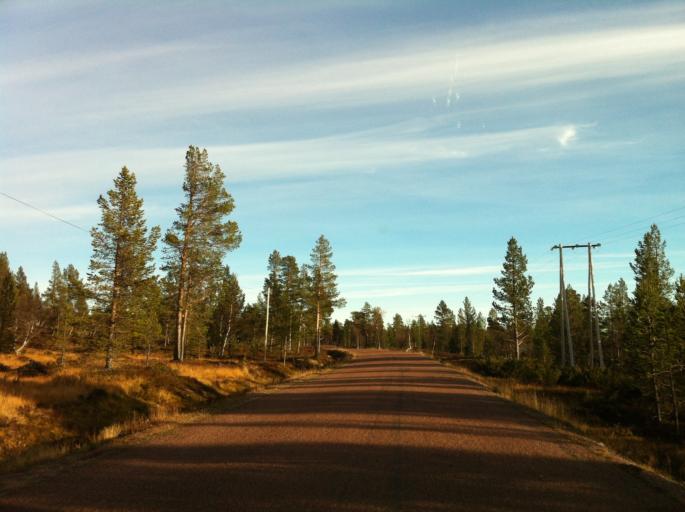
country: NO
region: Hedmark
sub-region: Engerdal
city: Engerdal
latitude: 62.0808
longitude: 12.1429
